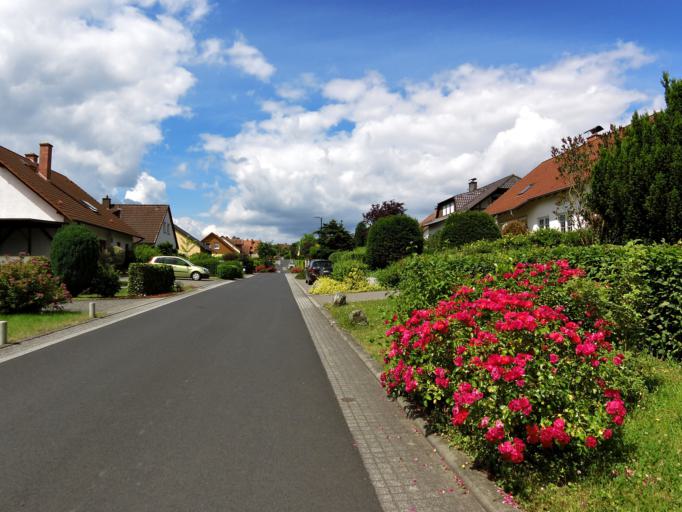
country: DE
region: Hesse
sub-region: Regierungsbezirk Kassel
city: Herleshausen
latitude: 51.0055
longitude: 10.1742
